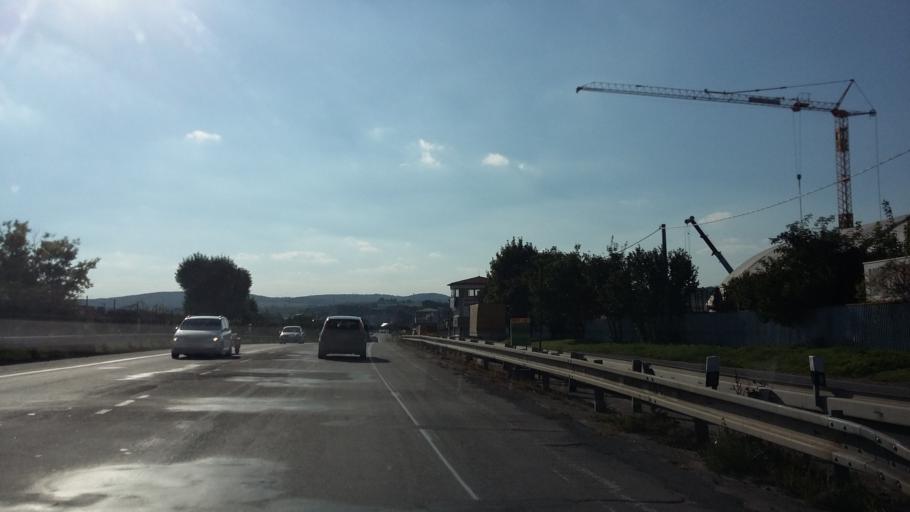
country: CZ
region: South Moravian
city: Ostopovice
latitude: 49.1732
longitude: 16.5484
